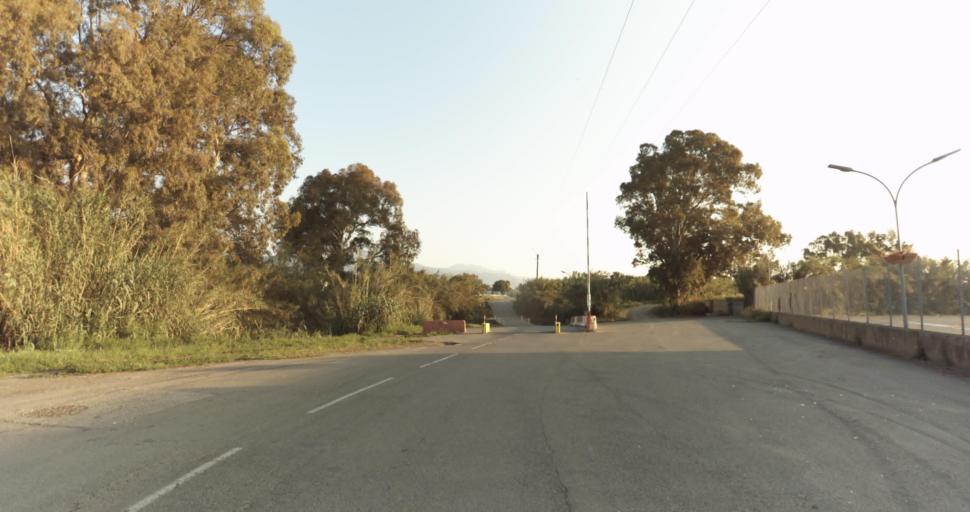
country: FR
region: Corsica
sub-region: Departement de la Haute-Corse
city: Biguglia
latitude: 42.6156
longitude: 9.4434
